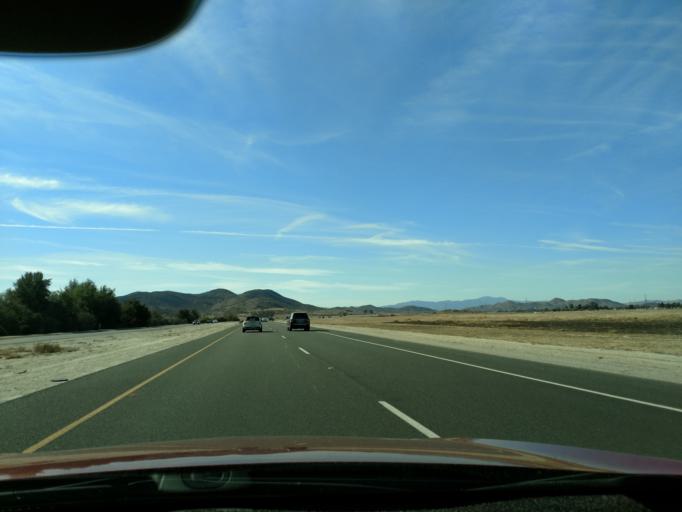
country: US
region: California
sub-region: Riverside County
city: Winchester
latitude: 33.6975
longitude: -117.0653
